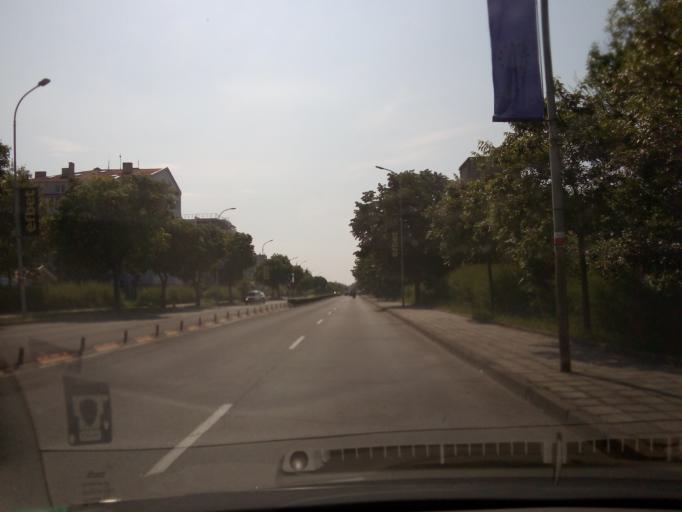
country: BG
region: Burgas
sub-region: Obshtina Pomorie
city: Pomorie
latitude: 42.5640
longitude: 27.6264
